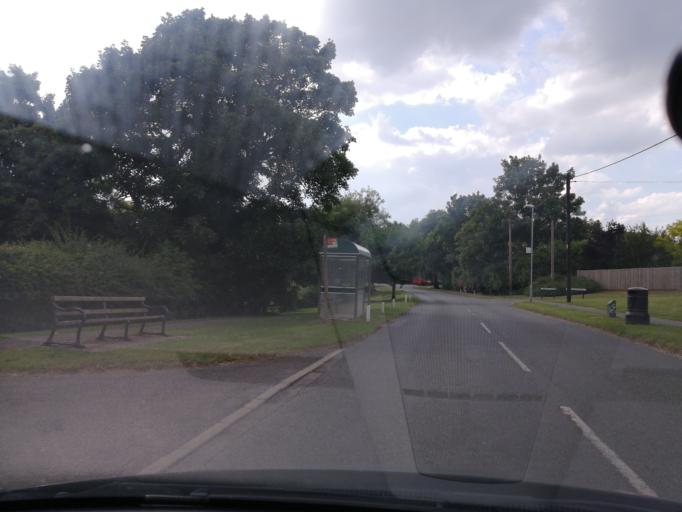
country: GB
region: England
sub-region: Cambridgeshire
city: Yaxley
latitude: 52.5124
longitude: -0.2680
